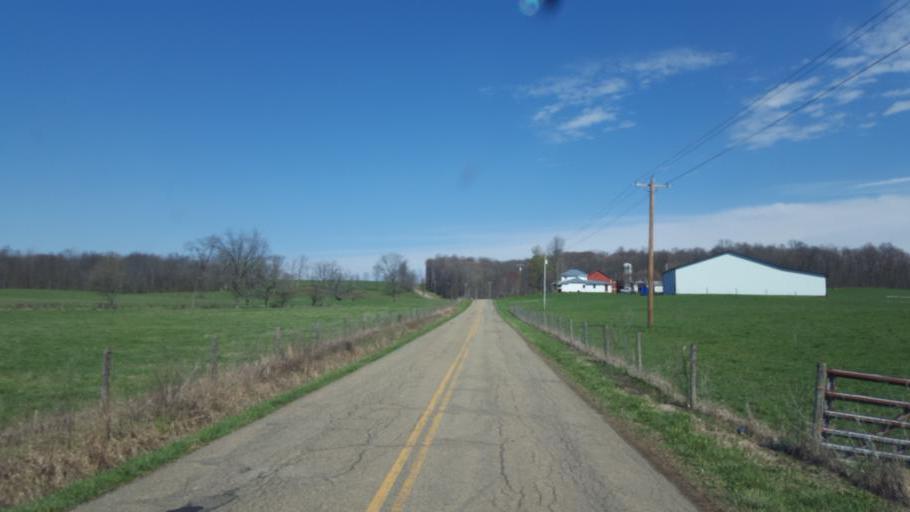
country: US
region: Ohio
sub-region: Knox County
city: Gambier
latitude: 40.3458
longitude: -82.3607
